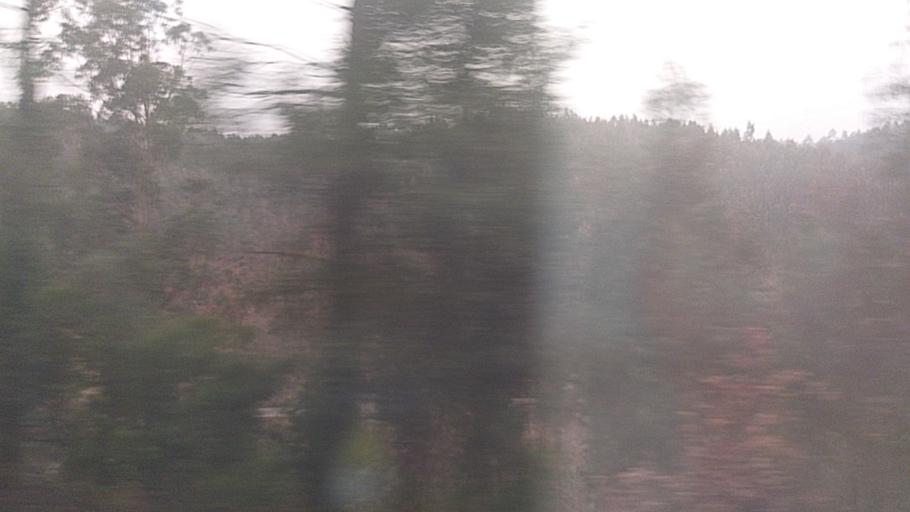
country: PT
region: Viseu
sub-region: Mortagua
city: Mortagua
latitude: 40.4154
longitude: -8.3062
